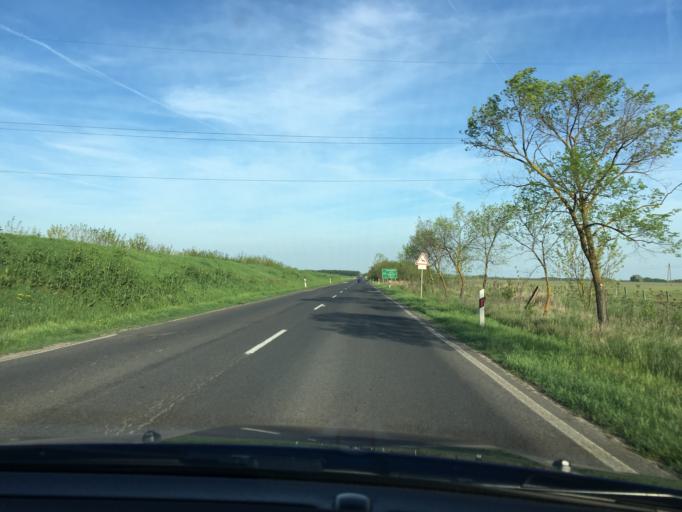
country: HU
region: Bekes
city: Szeghalom
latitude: 47.0104
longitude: 21.1894
